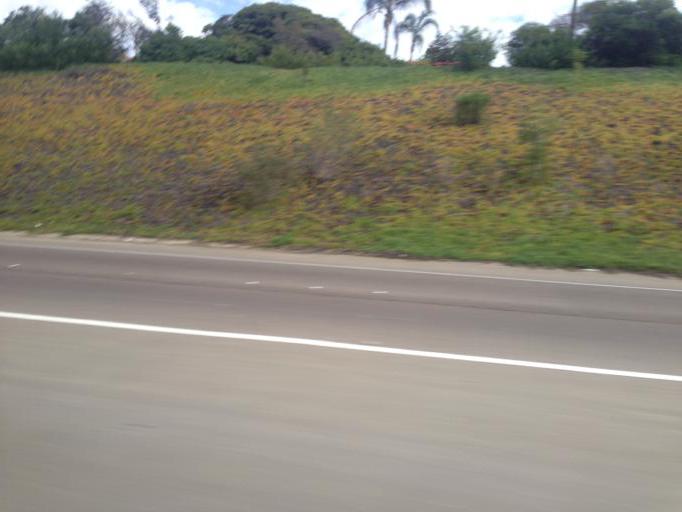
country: US
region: California
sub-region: San Diego County
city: Bonita
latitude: 32.6085
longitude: -117.0362
